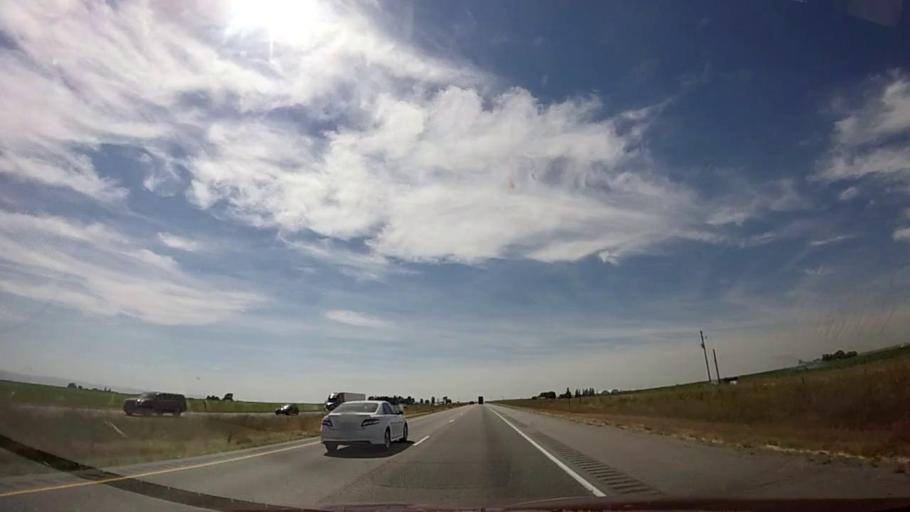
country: US
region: Idaho
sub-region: Cassia County
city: Burley
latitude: 42.5764
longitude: -113.9818
